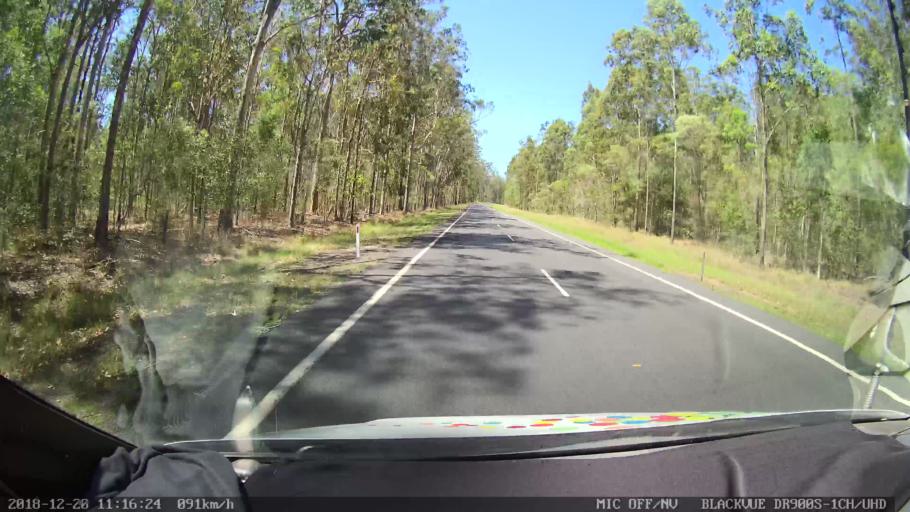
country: AU
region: New South Wales
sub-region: Richmond Valley
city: Casino
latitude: -29.0262
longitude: 153.0105
